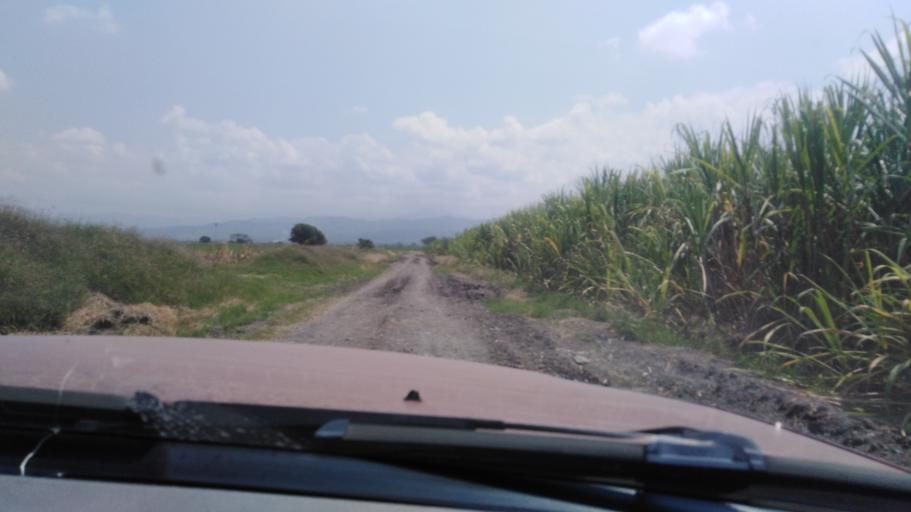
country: CO
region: Valle del Cauca
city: San Pedro
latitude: 3.9993
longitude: -76.2786
